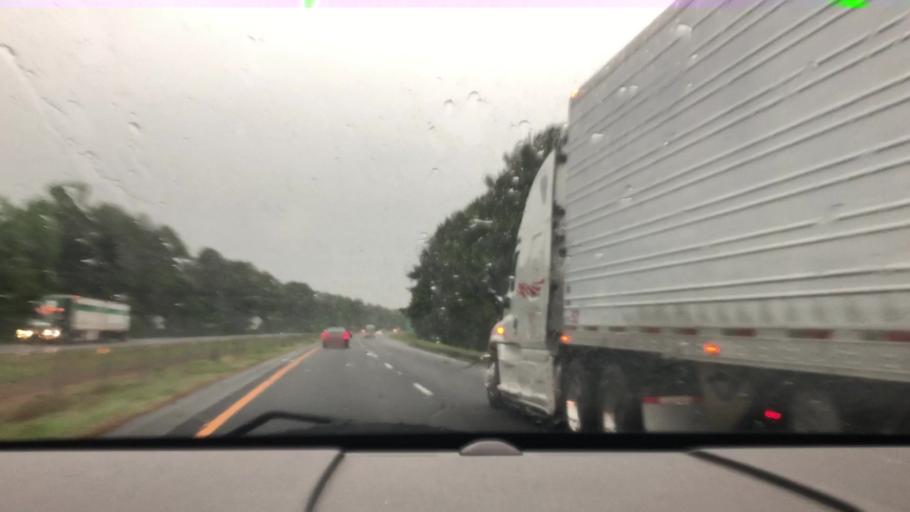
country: US
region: Alabama
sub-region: Butler County
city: Georgiana
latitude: 31.6629
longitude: -86.7647
